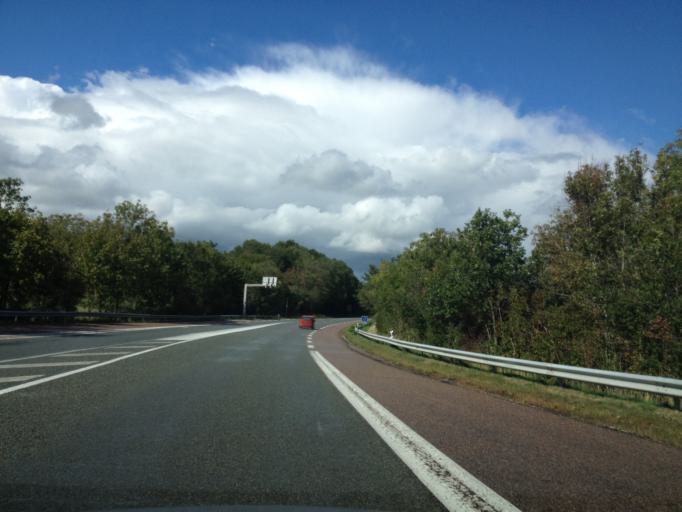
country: FR
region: Rhone-Alpes
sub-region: Departement du Rhone
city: Amplepuis
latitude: 45.9294
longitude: 4.3056
